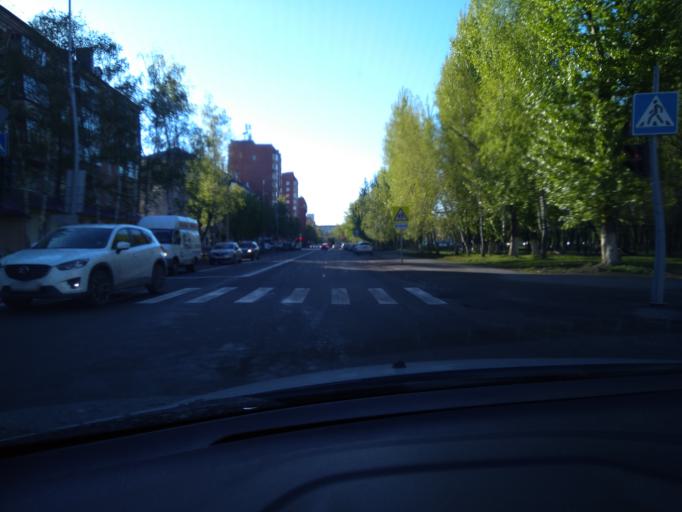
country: RU
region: Tjumen
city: Tyumen
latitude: 57.1327
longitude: 65.5851
